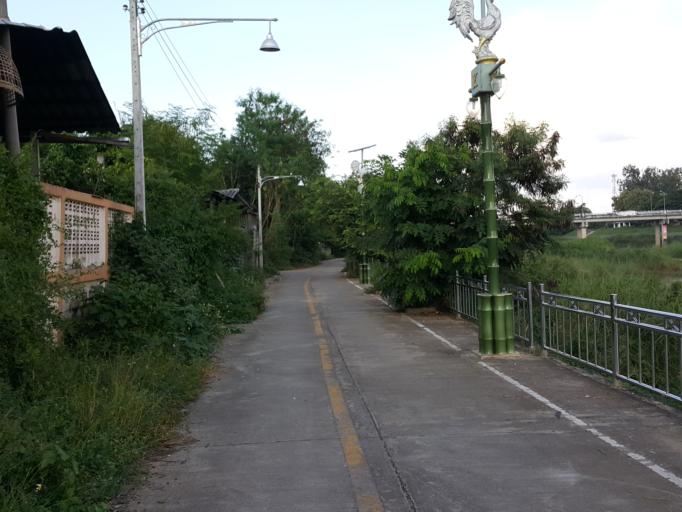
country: TH
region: Lampang
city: Lampang
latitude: 18.3022
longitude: 99.5111
